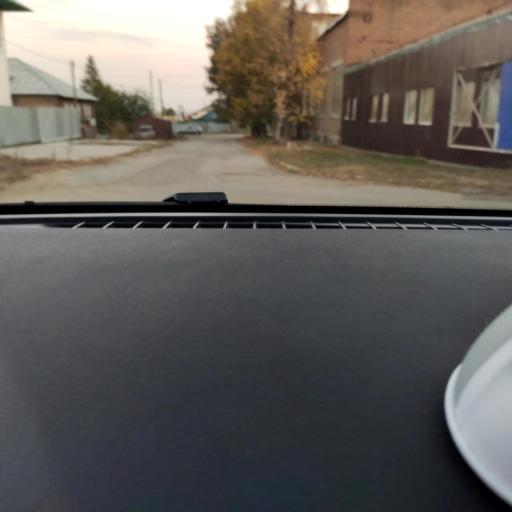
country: RU
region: Samara
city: Samara
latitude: 53.1798
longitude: 50.2004
